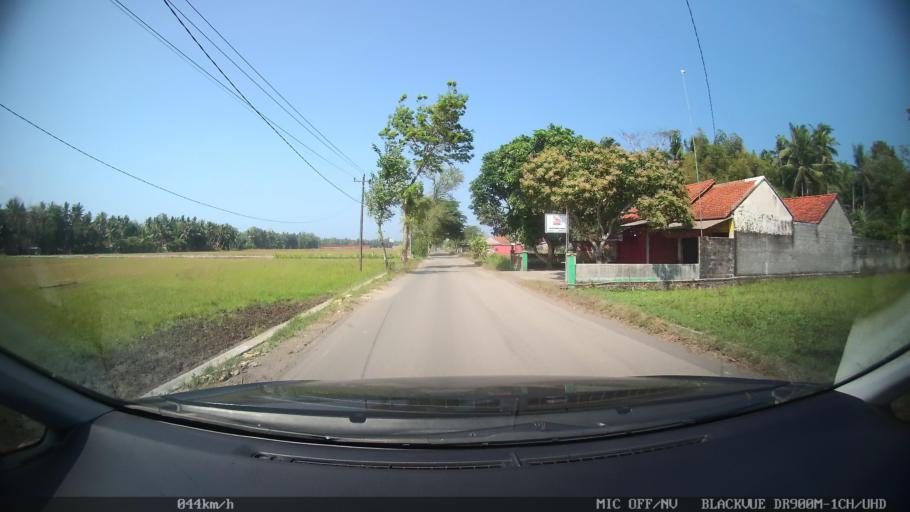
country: ID
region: Daerah Istimewa Yogyakarta
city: Srandakan
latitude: -7.9520
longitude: 110.2186
